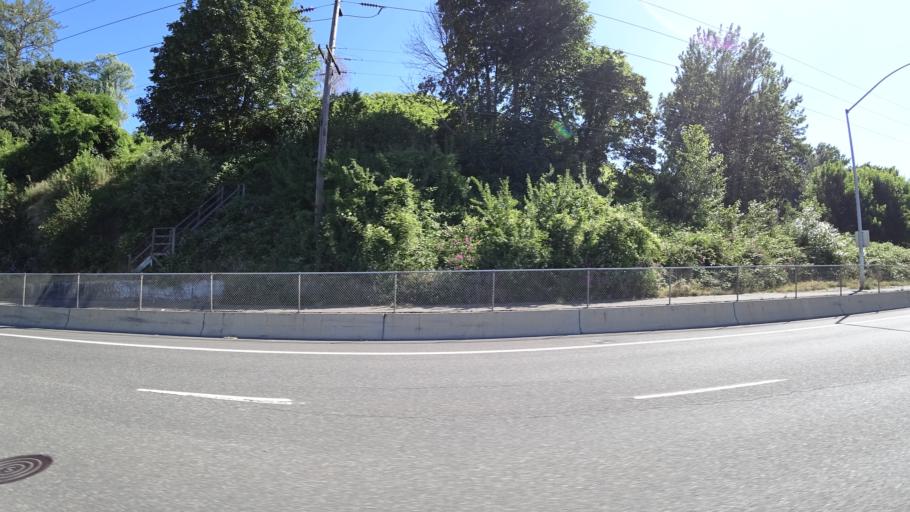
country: US
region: Oregon
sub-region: Multnomah County
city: Portland
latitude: 45.5464
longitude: -122.6826
